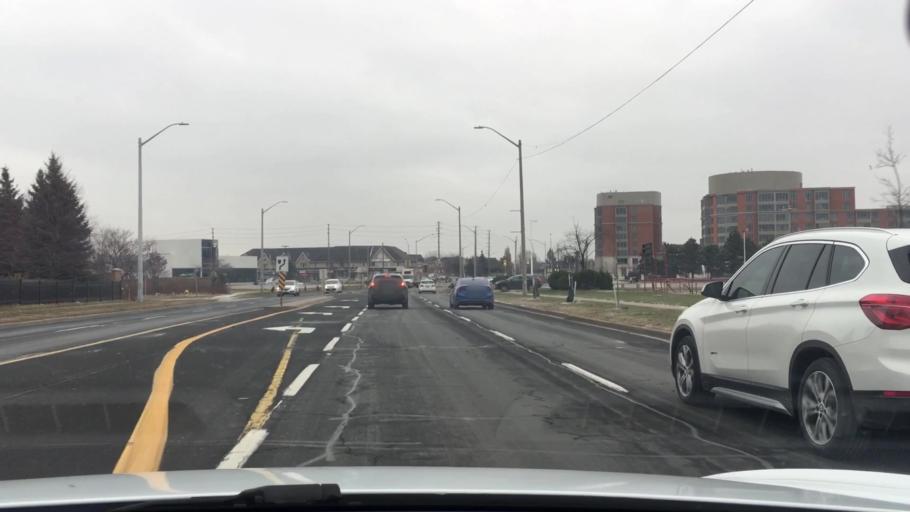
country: CA
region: Ontario
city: Markham
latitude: 43.8349
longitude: -79.3072
